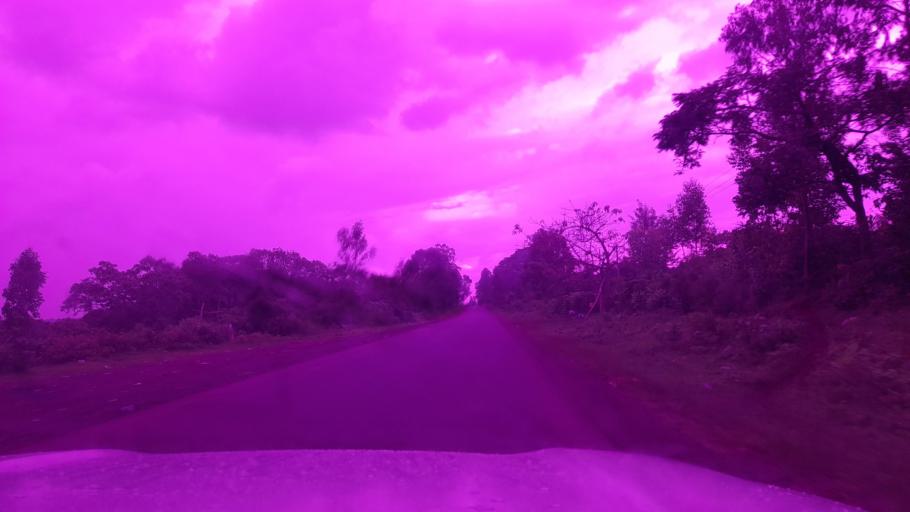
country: ET
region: Oromiya
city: Jima
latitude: 7.7087
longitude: 37.0558
